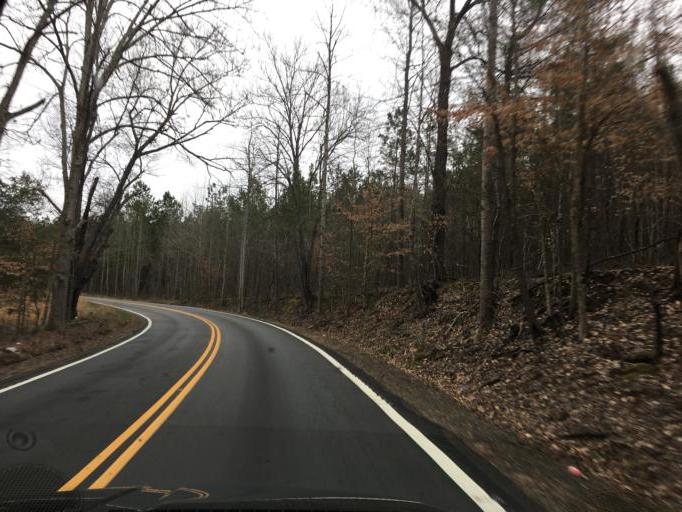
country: US
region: South Carolina
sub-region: Greenville County
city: Berea
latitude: 34.9304
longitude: -82.5057
